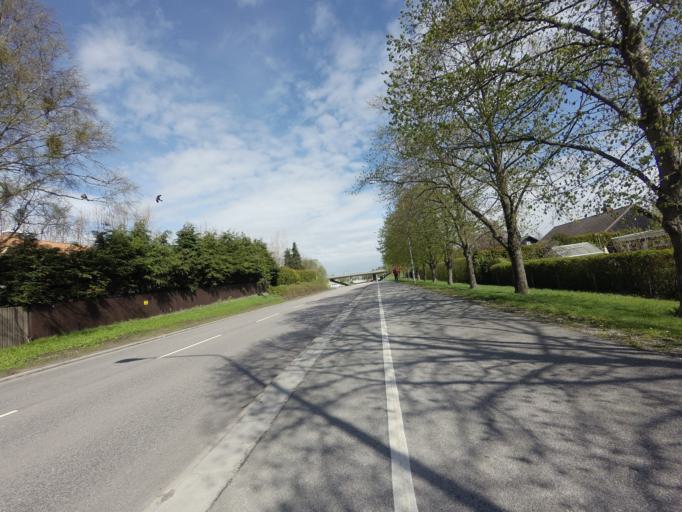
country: SE
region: Skane
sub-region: Vellinge Kommun
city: Vellinge
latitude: 55.4781
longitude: 13.0160
